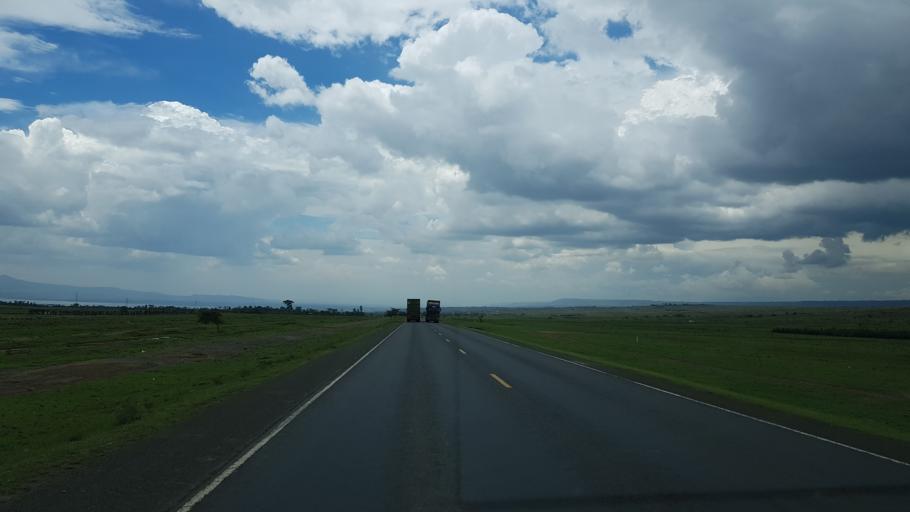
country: KE
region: Nakuru
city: Naivasha
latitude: -0.8407
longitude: 36.4750
